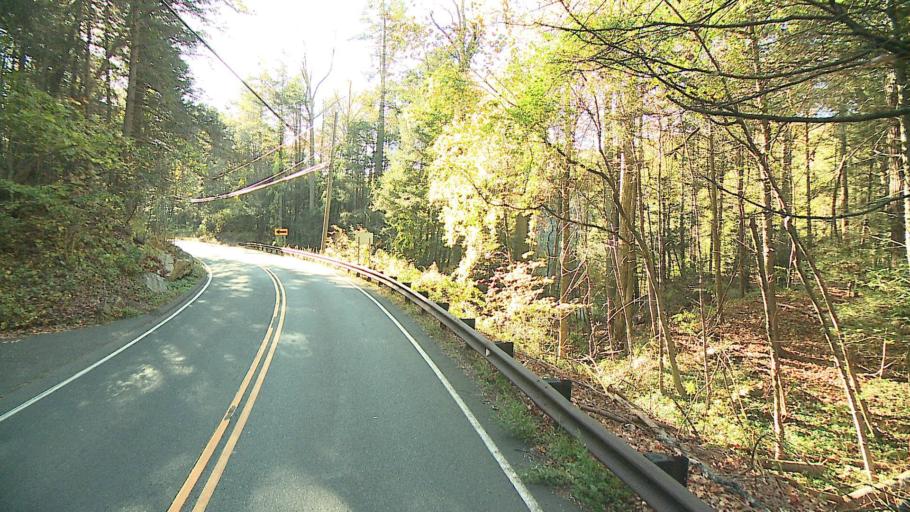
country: US
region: Connecticut
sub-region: Fairfield County
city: Georgetown
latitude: 41.2890
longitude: -73.3909
